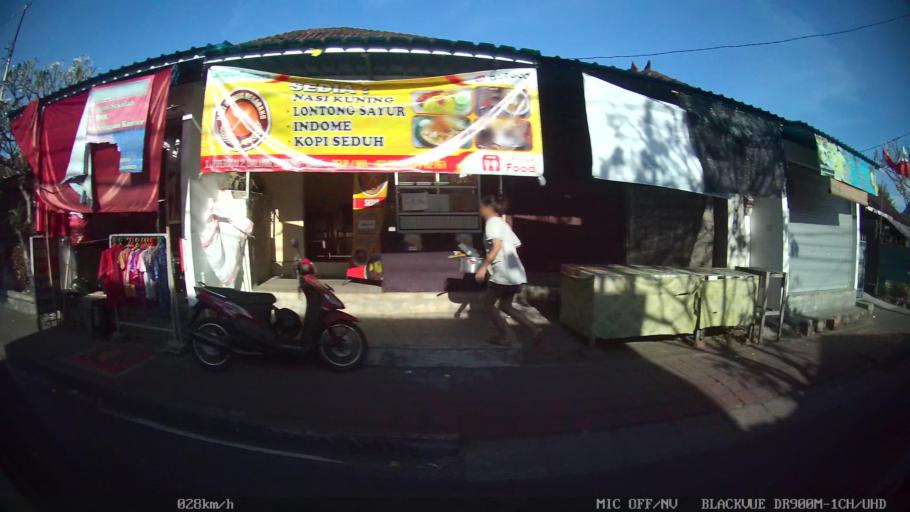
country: ID
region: Bali
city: Banjar Gunungpande
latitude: -8.6166
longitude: 115.1692
